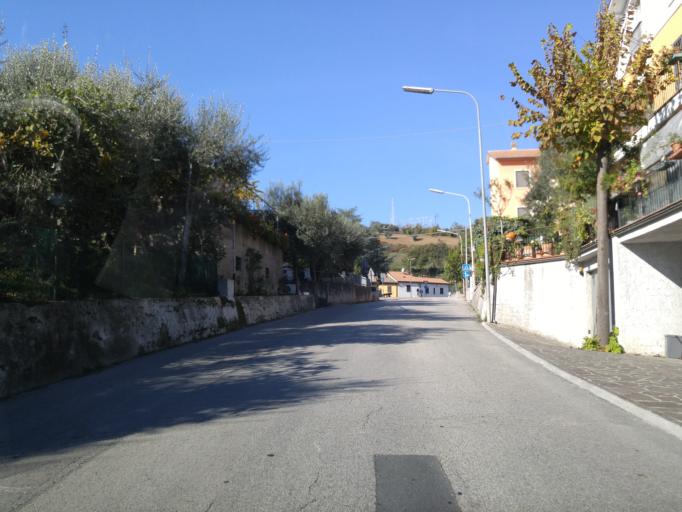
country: IT
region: The Marches
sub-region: Provincia di Pesaro e Urbino
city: Tavernelle
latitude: 43.7326
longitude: 12.8865
